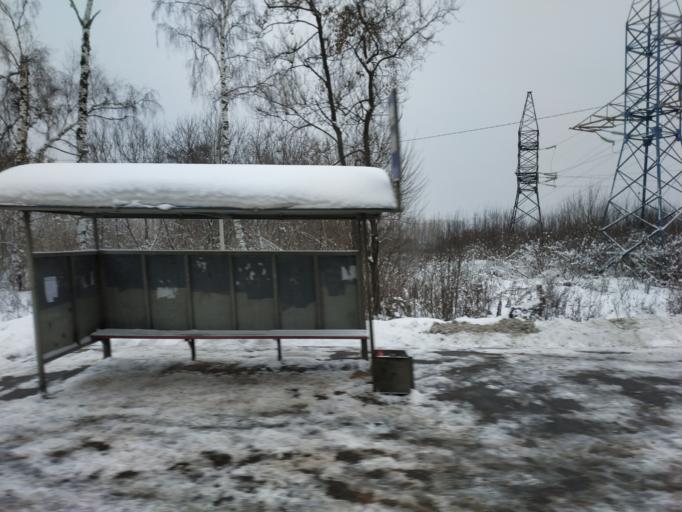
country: RU
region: Moskovskaya
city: Medvezh'i Ozera
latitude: 55.8468
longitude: 37.9610
